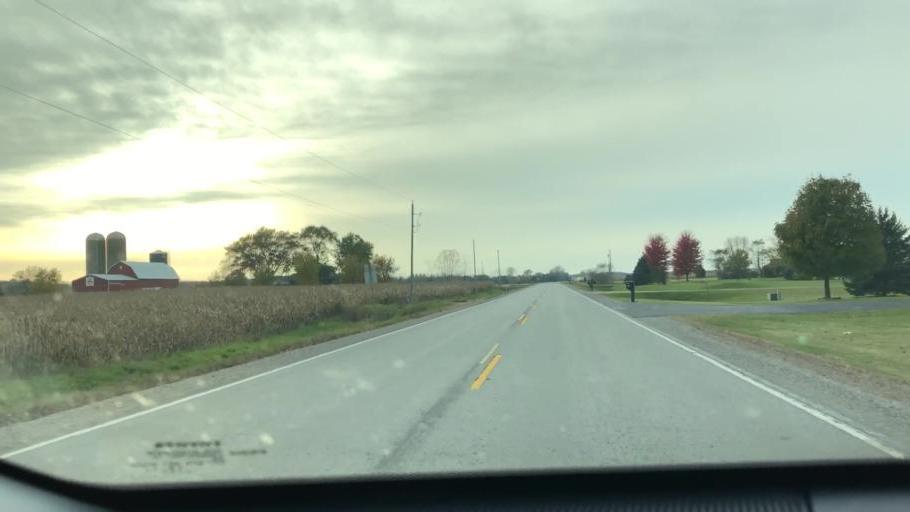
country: US
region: Wisconsin
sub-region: Outagamie County
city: Seymour
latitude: 44.4436
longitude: -88.3341
